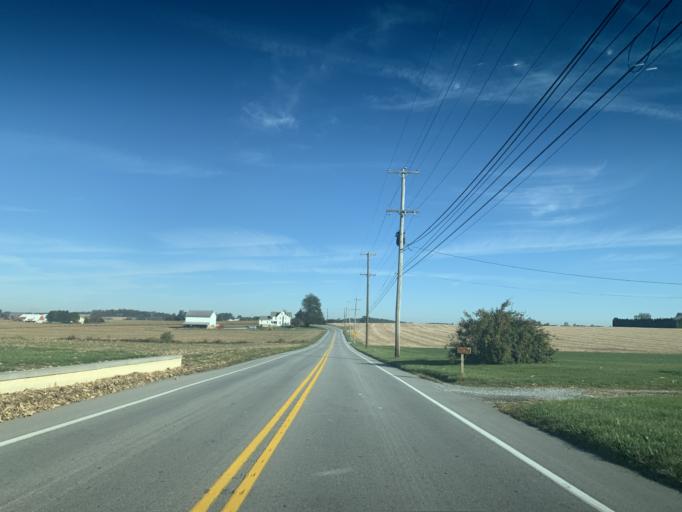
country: US
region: Pennsylvania
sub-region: Chester County
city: Parkesburg
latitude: 39.9097
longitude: -75.9100
